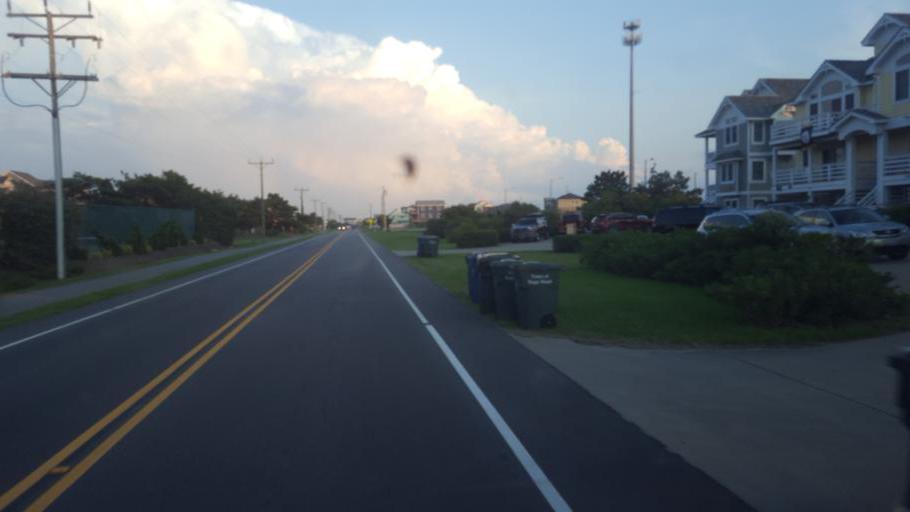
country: US
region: North Carolina
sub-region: Dare County
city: Nags Head
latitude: 35.9357
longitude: -75.6120
